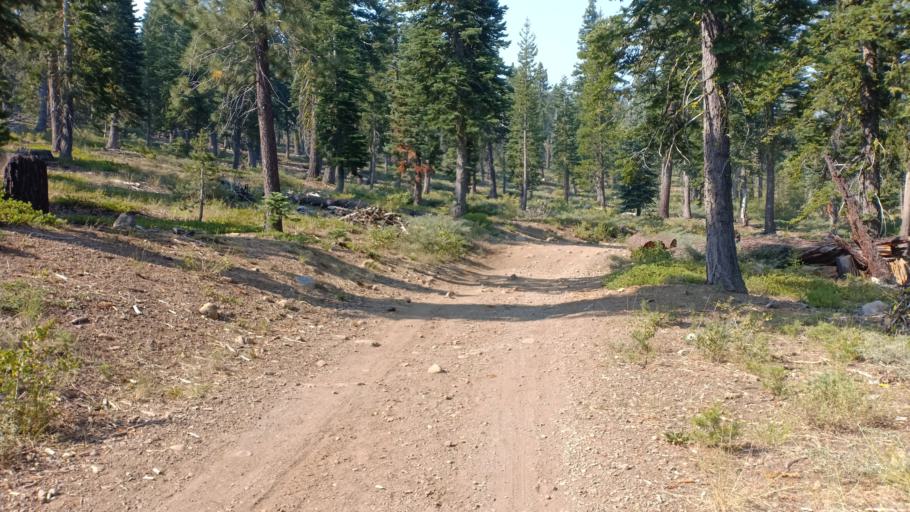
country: US
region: California
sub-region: Placer County
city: Sunnyside-Tahoe City
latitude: 39.1465
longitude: -120.1781
